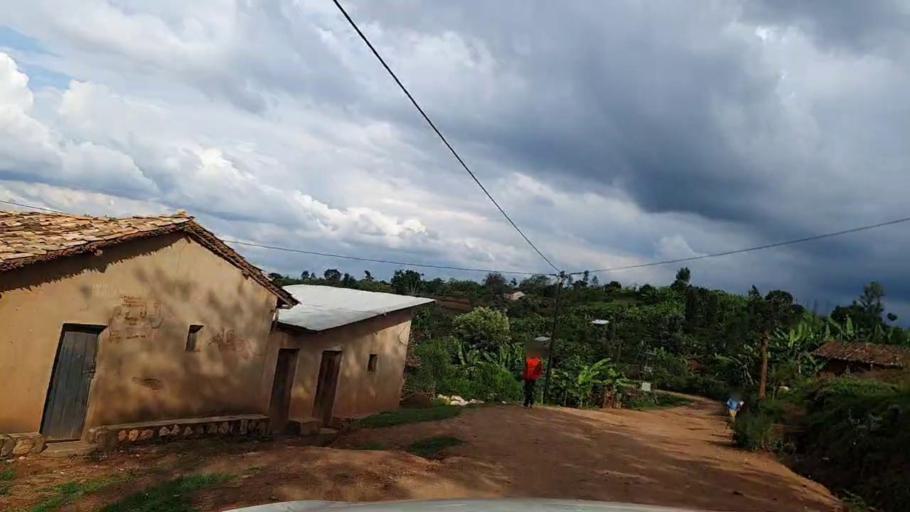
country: RW
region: Southern Province
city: Gikongoro
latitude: -2.4241
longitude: 29.6444
